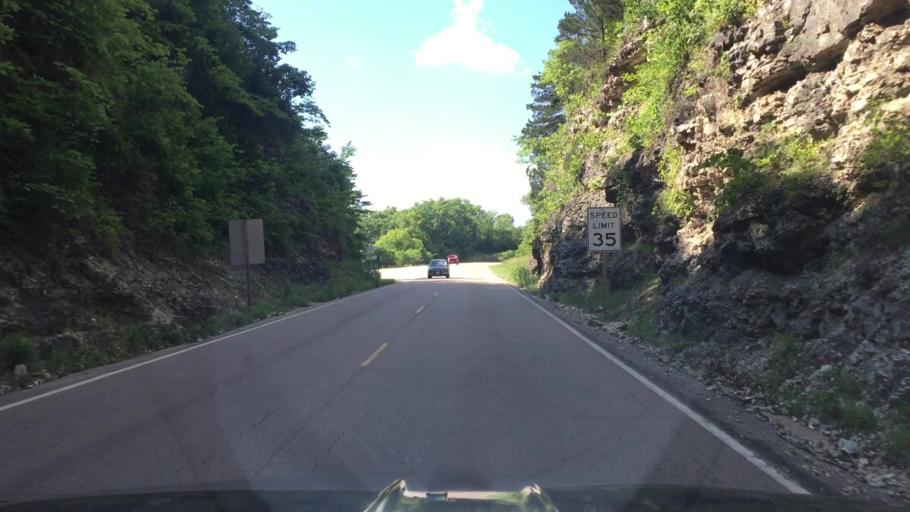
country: US
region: Missouri
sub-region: Miller County
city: Lake Ozark
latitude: 38.2075
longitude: -92.6227
